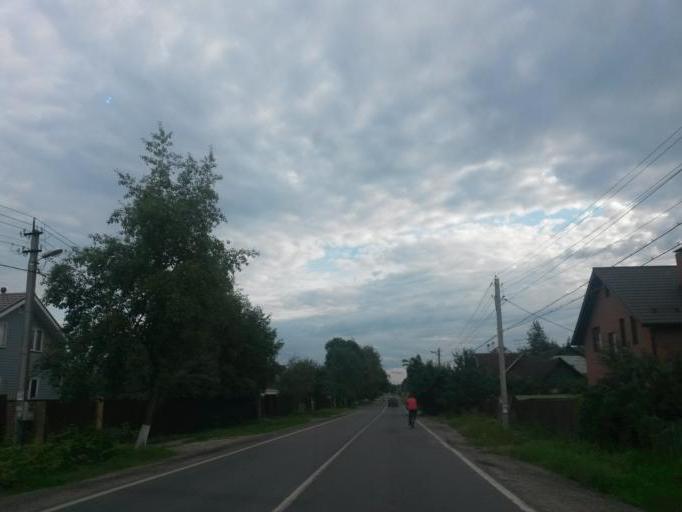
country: RU
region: Moskovskaya
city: Vostryakovo
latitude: 55.4056
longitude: 37.8211
